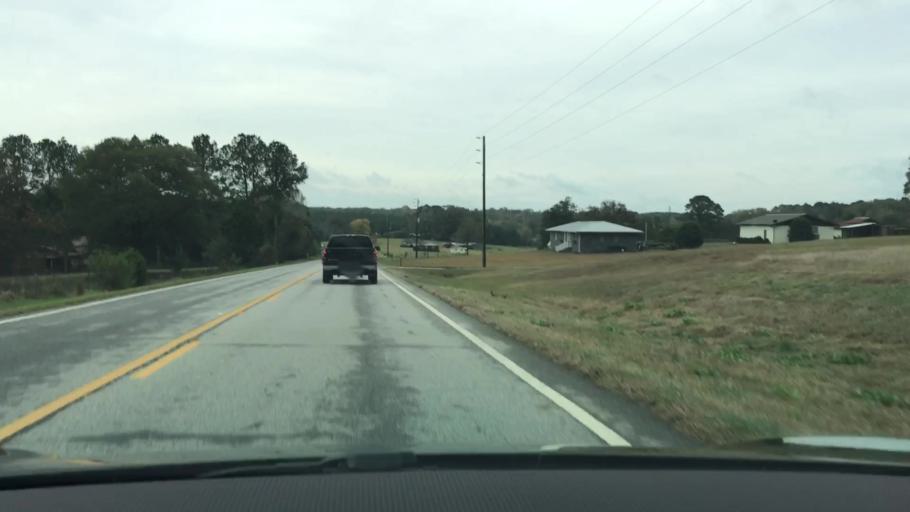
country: US
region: Georgia
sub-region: Greene County
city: Greensboro
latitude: 33.6492
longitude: -83.2346
